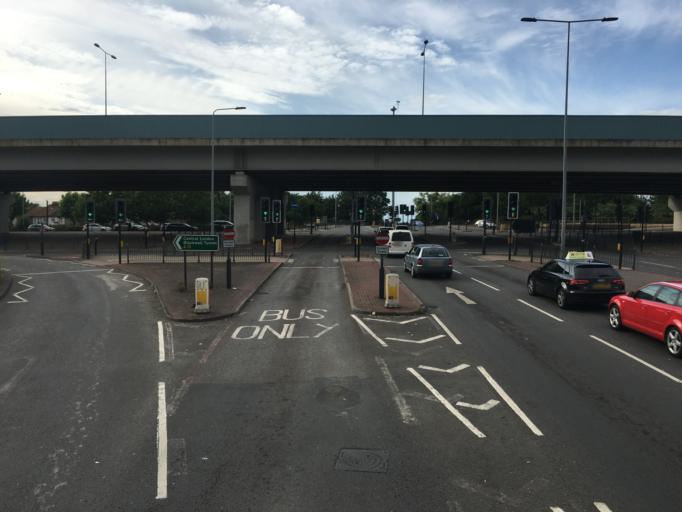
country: GB
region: England
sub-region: Greater London
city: East Ham
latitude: 51.5197
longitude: 0.0594
